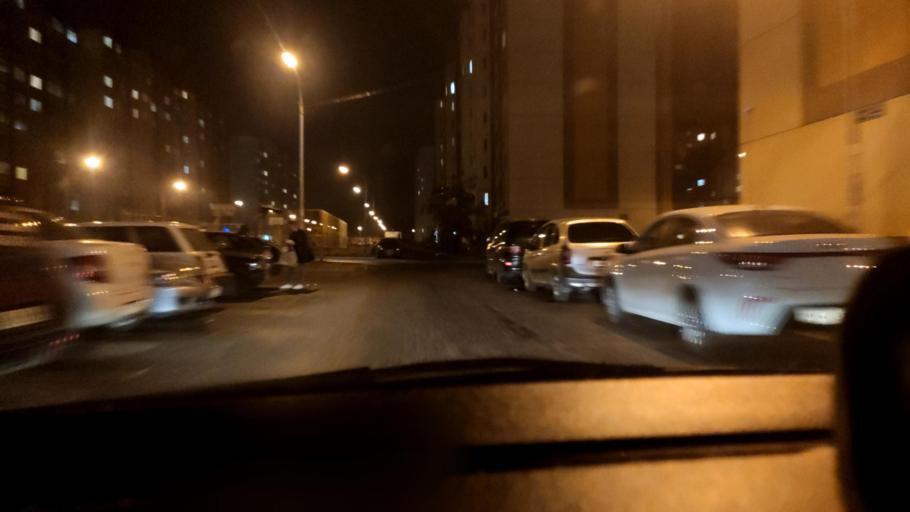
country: RU
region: Voronezj
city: Voronezh
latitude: 51.7141
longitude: 39.1868
